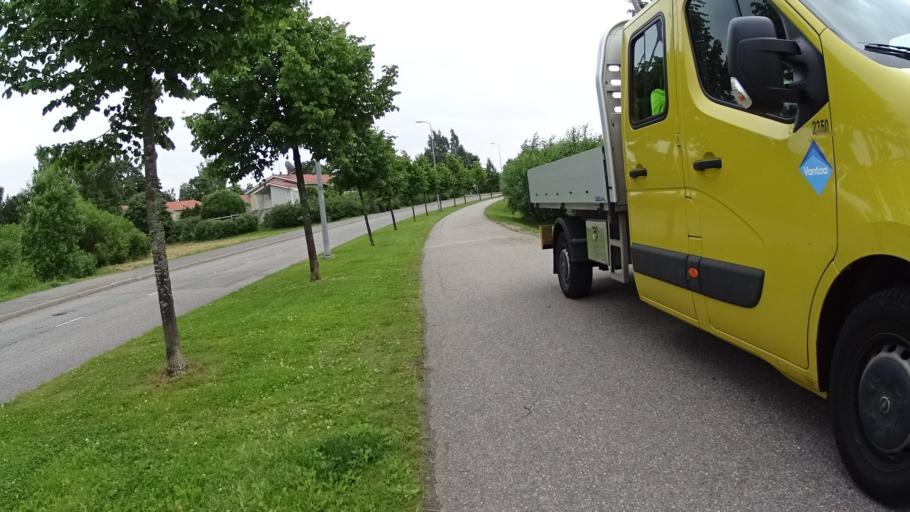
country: FI
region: Uusimaa
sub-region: Helsinki
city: Helsinki
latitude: 60.2771
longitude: 24.9122
